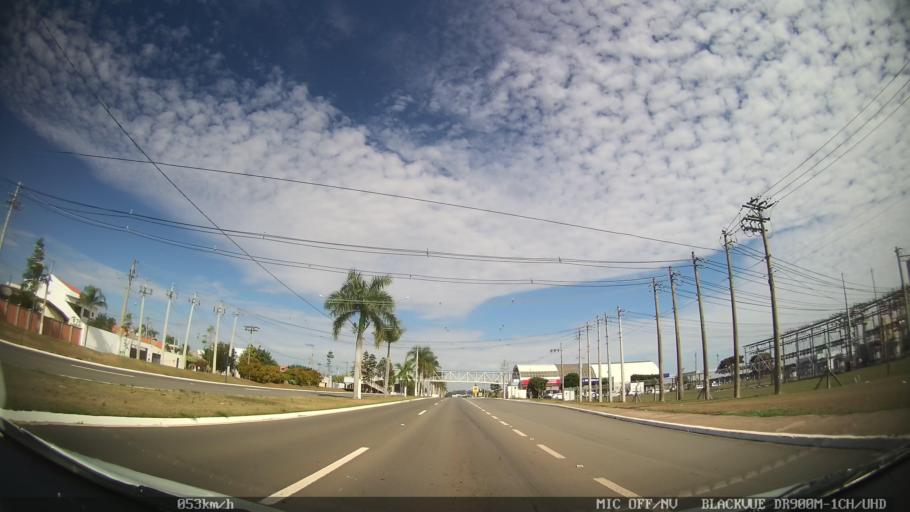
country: BR
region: Sao Paulo
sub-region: Santa Barbara D'Oeste
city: Santa Barbara d'Oeste
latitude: -22.7648
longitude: -47.4344
